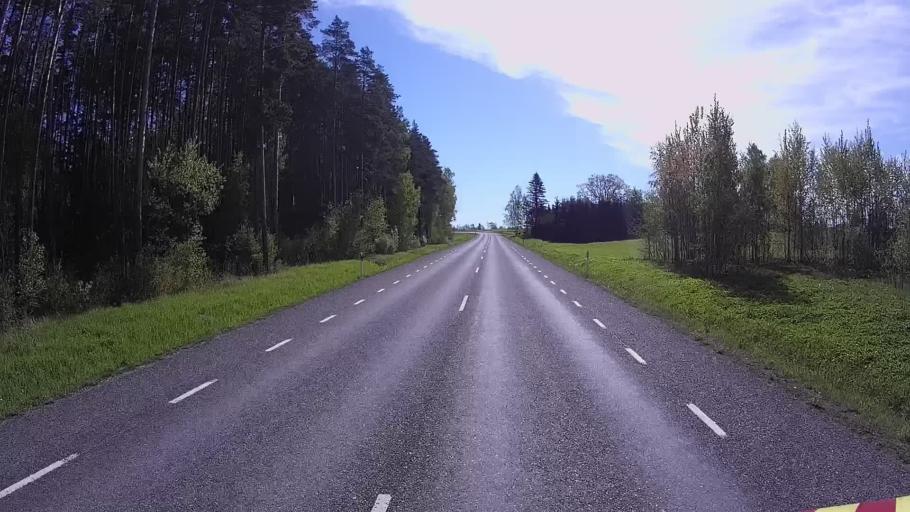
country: EE
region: Polvamaa
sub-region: Raepina vald
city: Rapina
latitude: 58.0956
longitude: 27.4204
